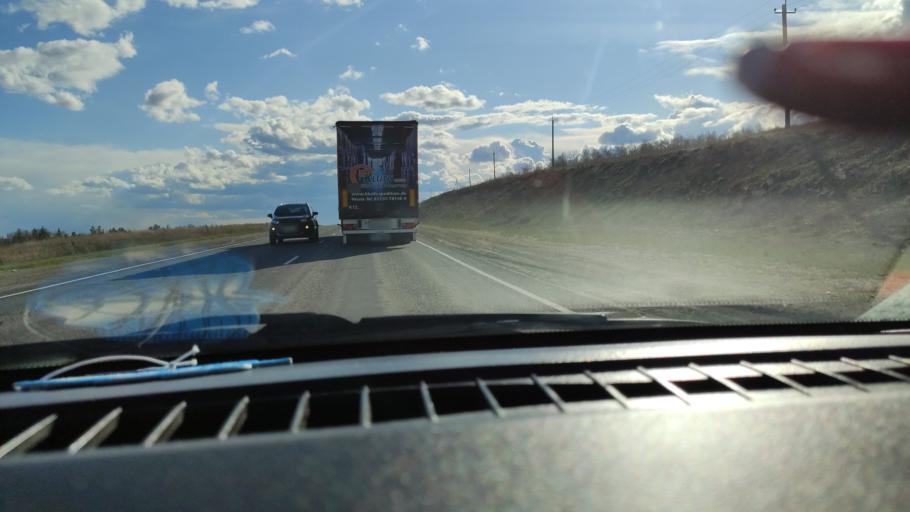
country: RU
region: Saratov
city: Sinodskoye
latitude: 52.0705
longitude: 46.7771
